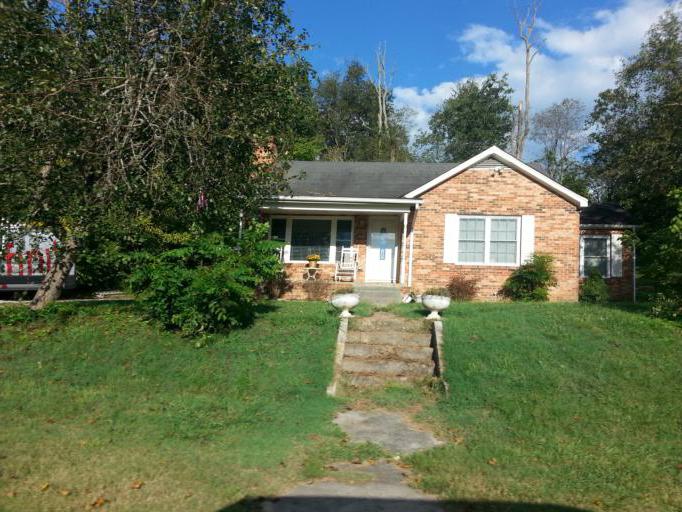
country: US
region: Tennessee
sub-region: Knox County
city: Mascot
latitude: 36.0998
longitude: -83.7870
